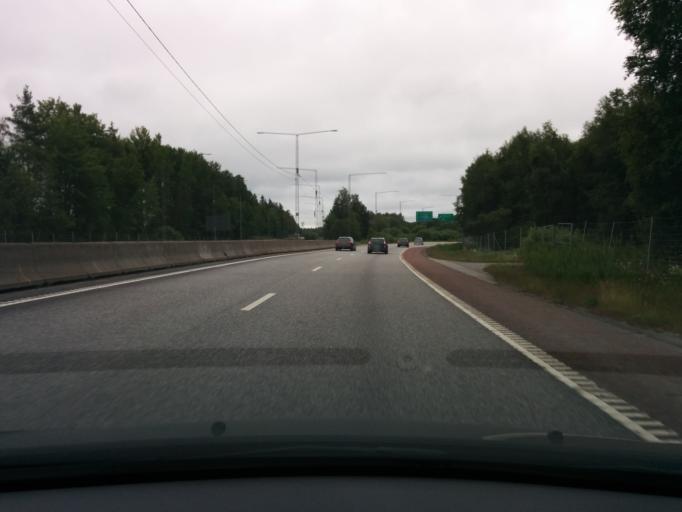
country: SE
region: Stockholm
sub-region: Sigtuna Kommun
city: Rosersberg
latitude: 59.6214
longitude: 17.9095
